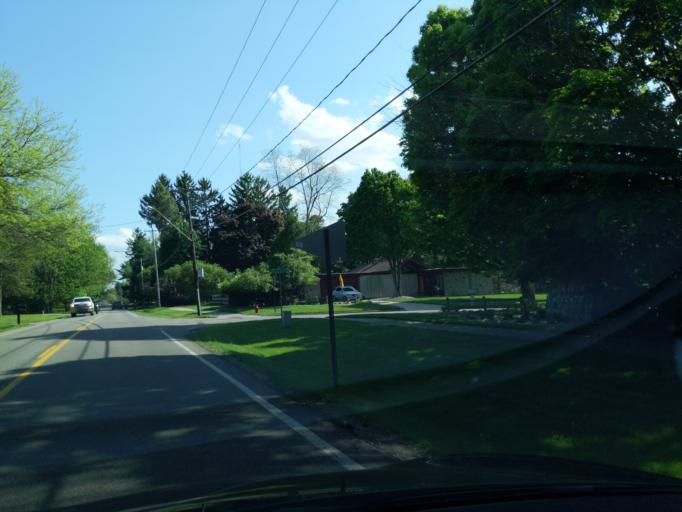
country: US
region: Michigan
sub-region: Ingham County
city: Okemos
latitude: 42.7113
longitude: -84.4104
